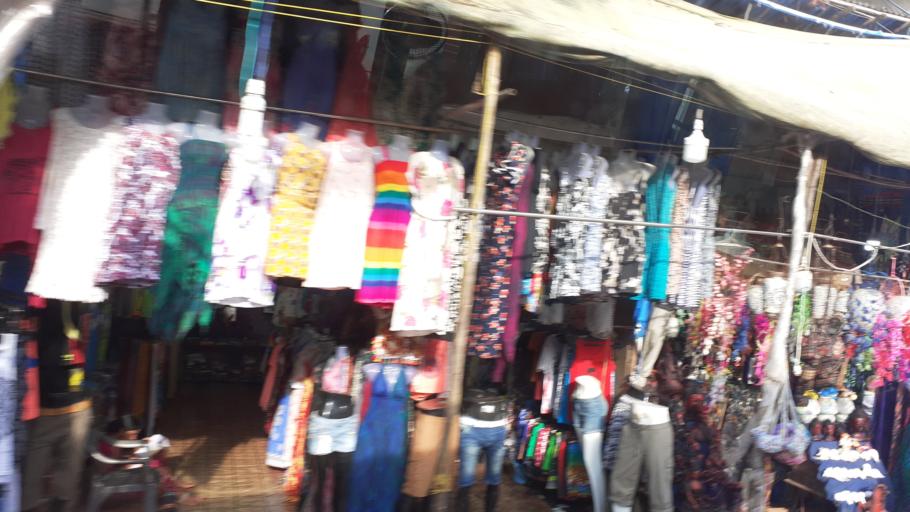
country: IN
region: Goa
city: Calangute
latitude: 15.5521
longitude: 73.7586
